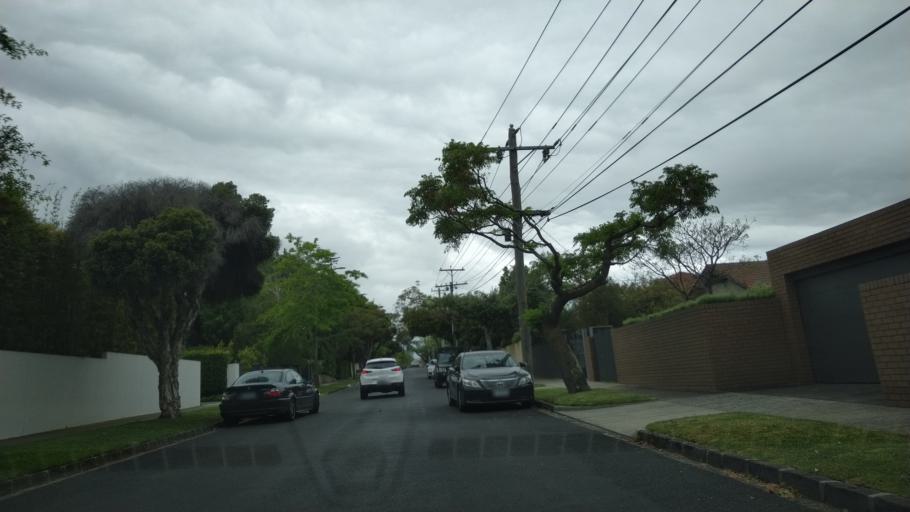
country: AU
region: Victoria
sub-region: Glen Eira
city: Caulfield
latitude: -37.8831
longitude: 145.0300
